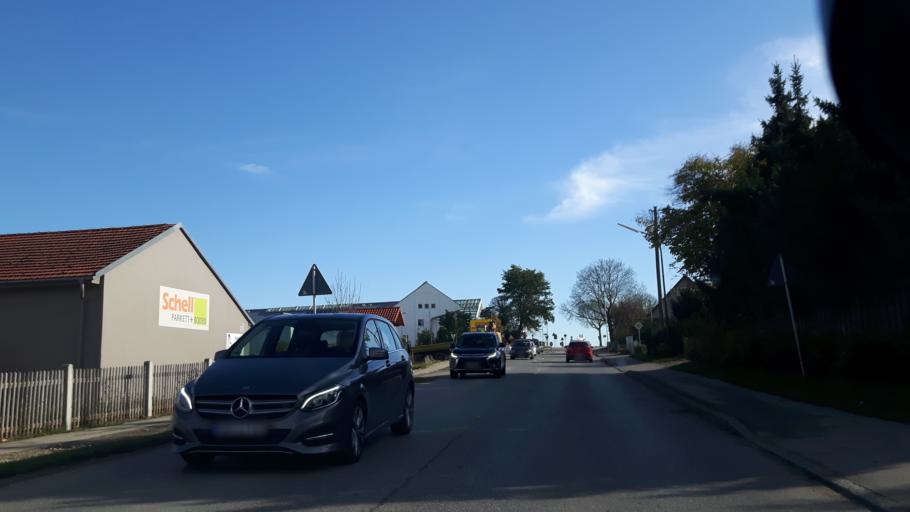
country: DE
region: Bavaria
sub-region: Upper Bavaria
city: Schwabhausen
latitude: 48.3011
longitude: 11.3657
